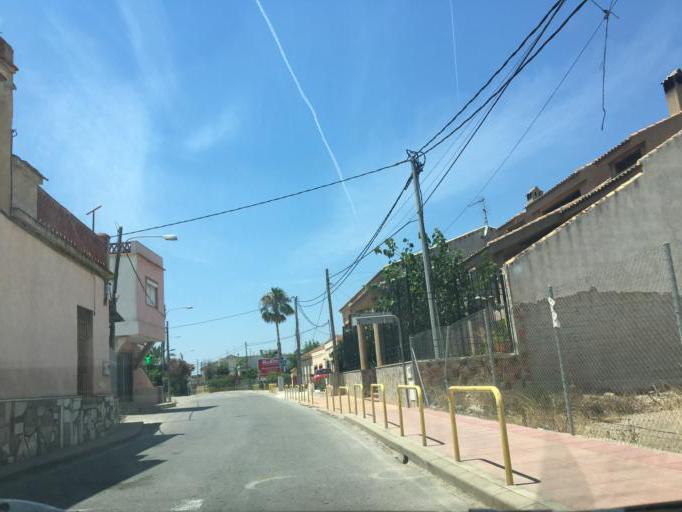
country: ES
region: Murcia
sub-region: Murcia
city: Santomera
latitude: 38.0329
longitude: -1.0615
